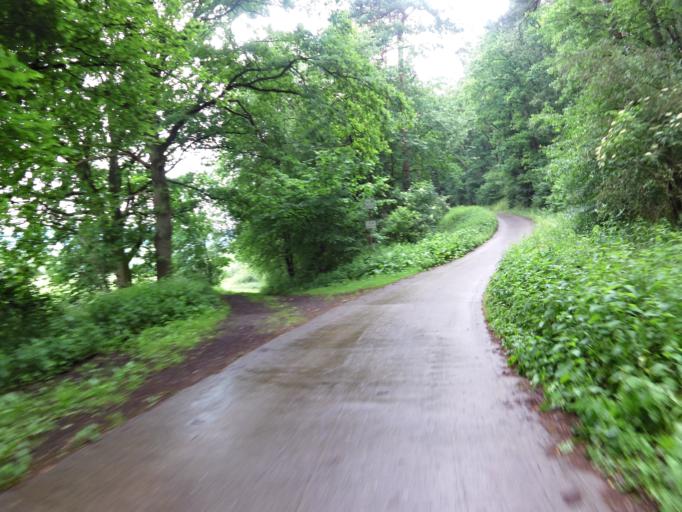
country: DE
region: Hesse
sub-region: Regierungsbezirk Kassel
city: Bad Hersfeld
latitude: 50.8744
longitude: 9.7286
